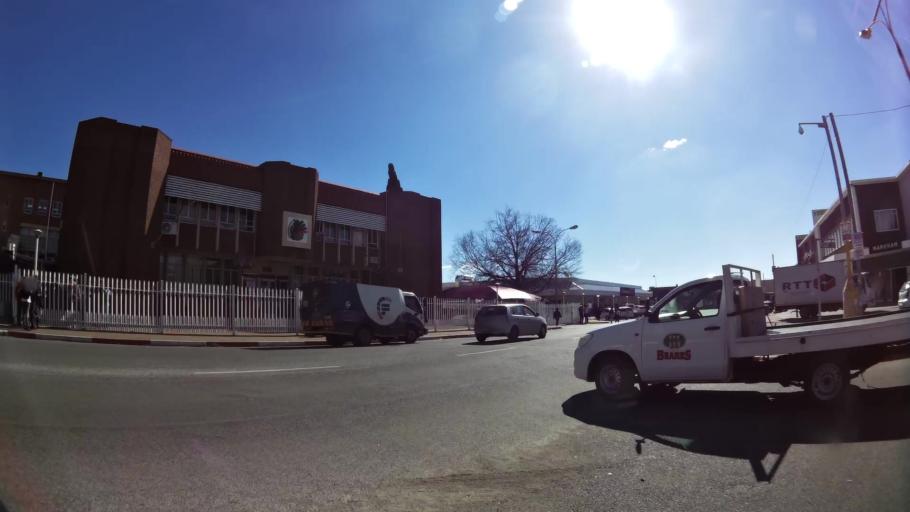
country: ZA
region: Gauteng
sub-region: West Rand District Municipality
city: Carletonville
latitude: -26.3573
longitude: 27.3978
